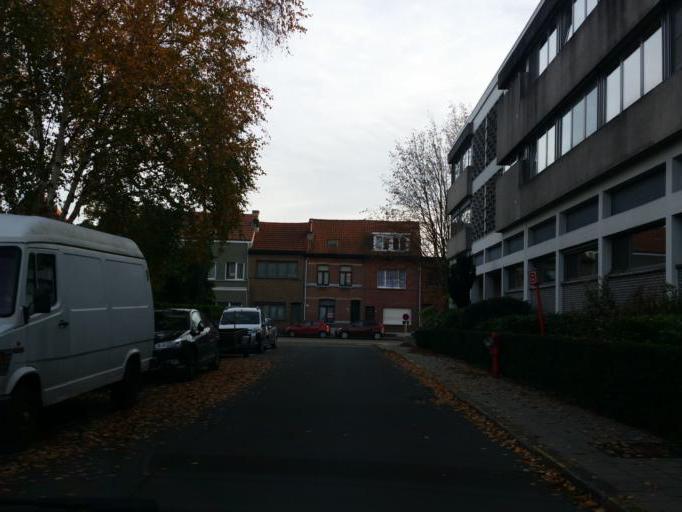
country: BE
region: Flanders
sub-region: Provincie Antwerpen
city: Hoboken
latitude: 51.1845
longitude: 4.3539
